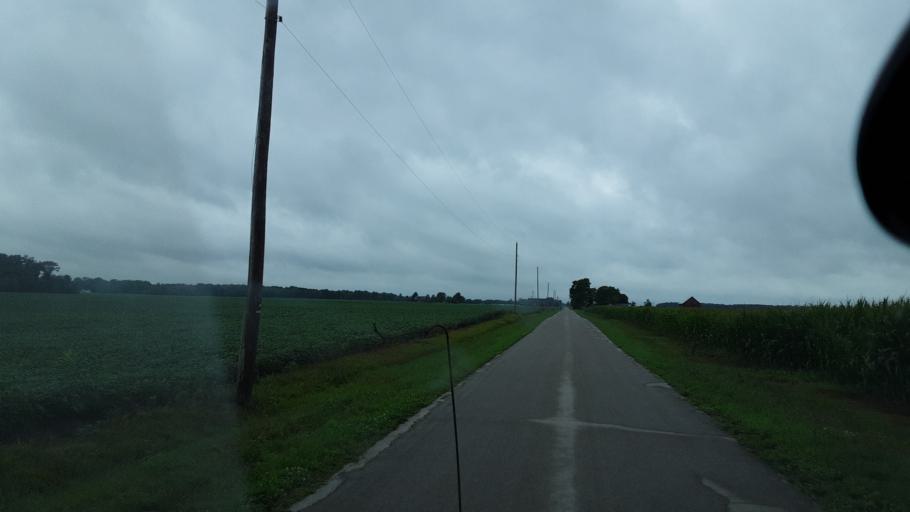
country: US
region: Ohio
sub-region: Van Wert County
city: Convoy
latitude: 40.8296
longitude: -84.7619
